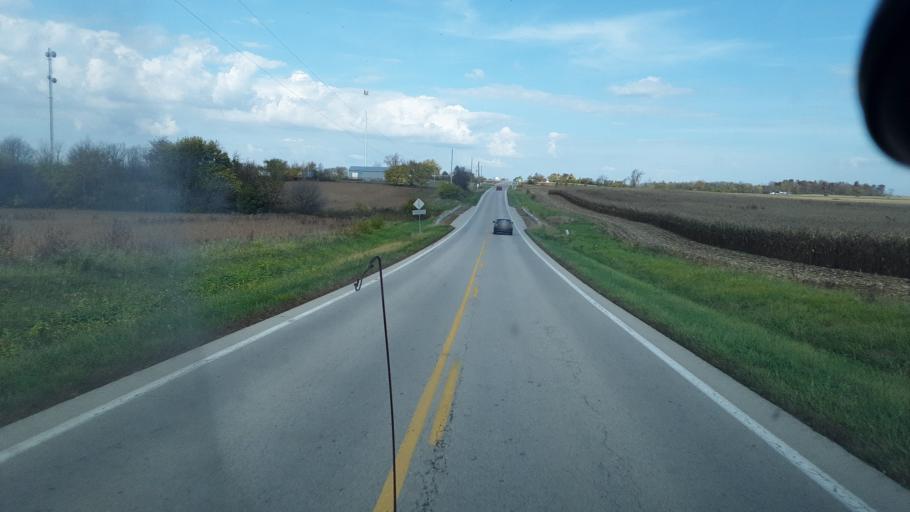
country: US
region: Ohio
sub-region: Clinton County
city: Sabina
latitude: 39.5506
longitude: -83.7151
